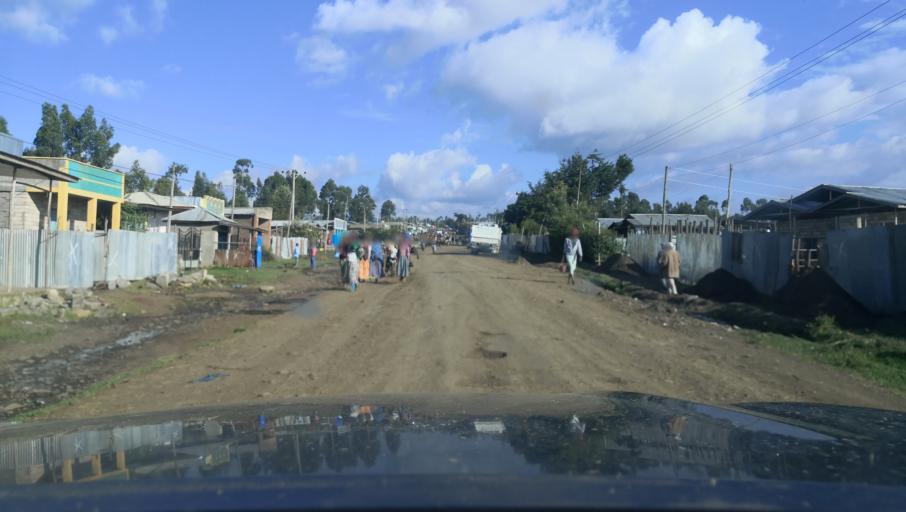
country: ET
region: Oromiya
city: Tulu Bolo
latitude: 8.4710
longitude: 38.2496
